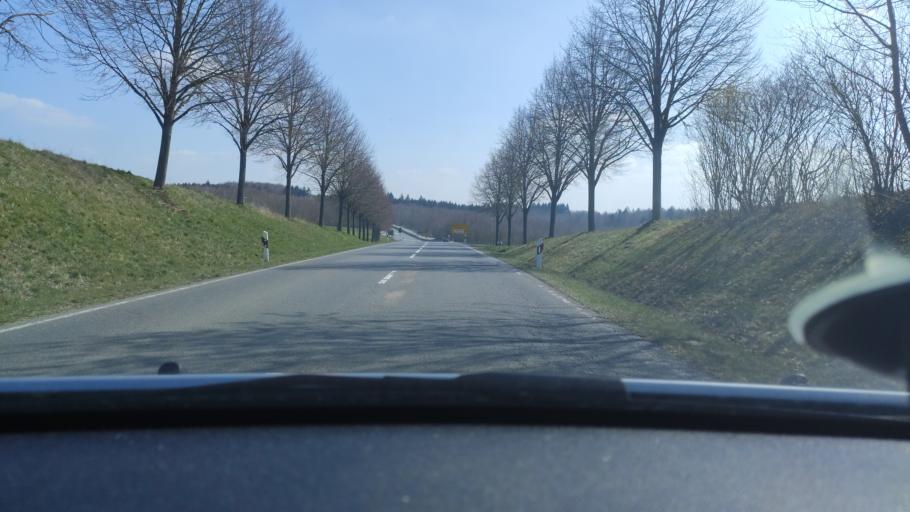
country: DE
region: Baden-Wuerttemberg
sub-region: Regierungsbezirk Stuttgart
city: Assamstadt
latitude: 49.4412
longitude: 9.7150
